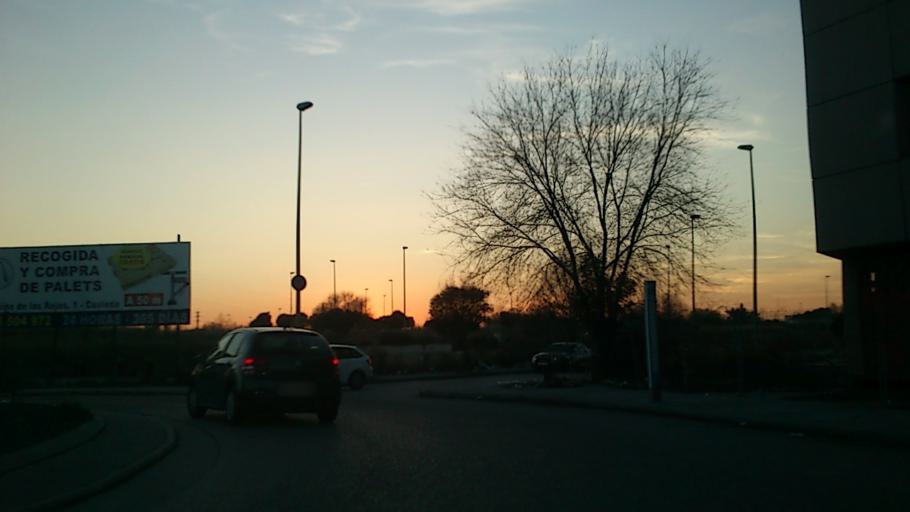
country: ES
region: Madrid
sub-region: Provincia de Madrid
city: San Fernando de Henares
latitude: 40.4448
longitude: -3.5410
